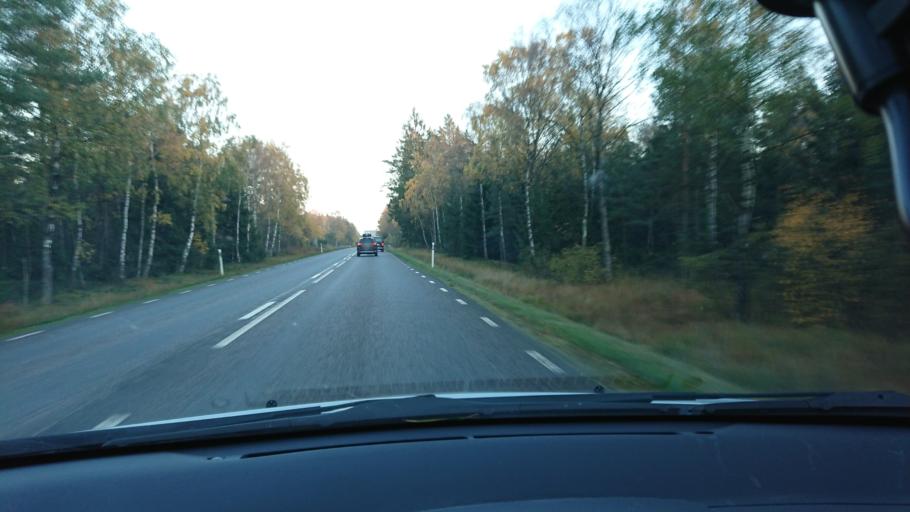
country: SE
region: Halland
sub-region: Laholms Kommun
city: Veinge
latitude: 56.7167
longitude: 13.1894
